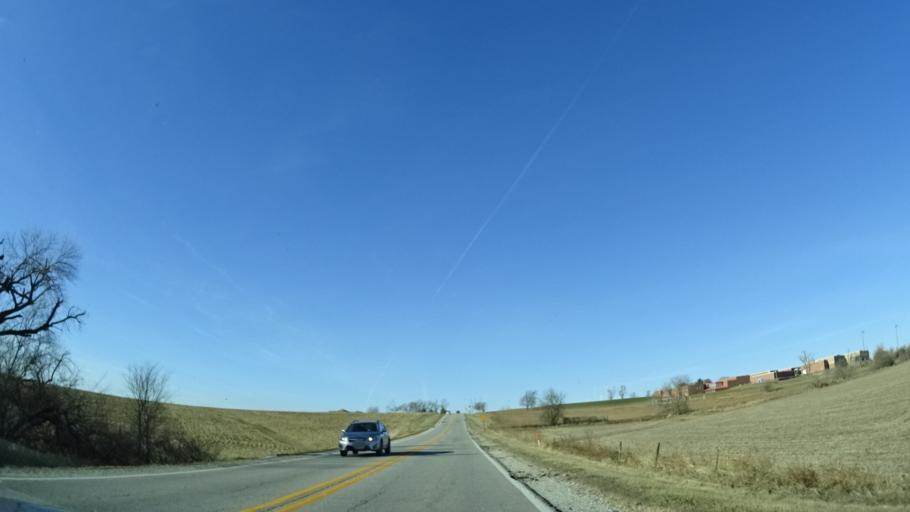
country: US
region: Nebraska
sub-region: Sarpy County
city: Springfield
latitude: 41.0890
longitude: -96.0743
